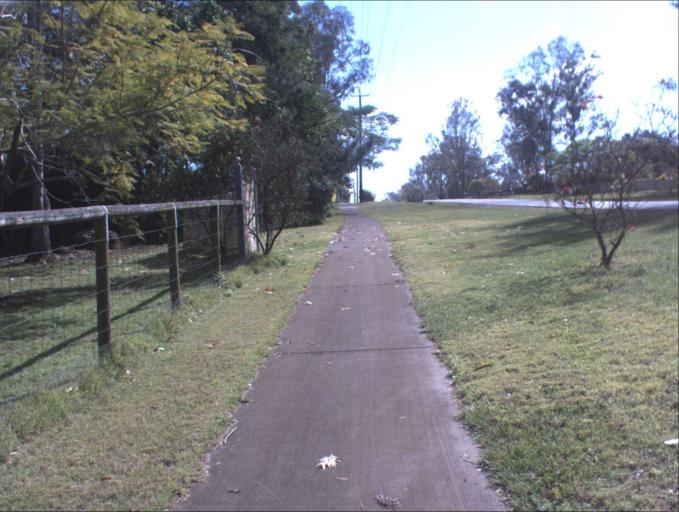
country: AU
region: Queensland
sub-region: Logan
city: Park Ridge South
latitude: -27.7162
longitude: 152.9766
